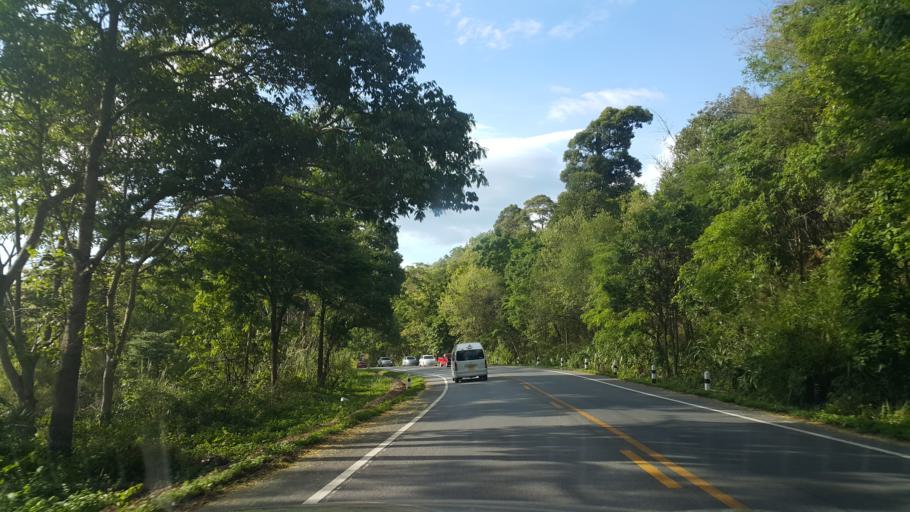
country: TH
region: Phayao
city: Phayao
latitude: 19.0643
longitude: 99.7725
